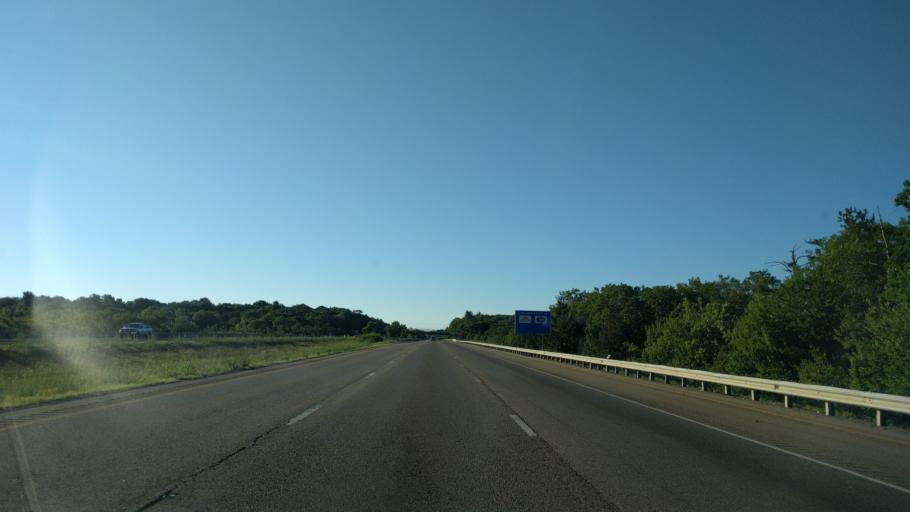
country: US
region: Massachusetts
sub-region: Norfolk County
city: Franklin
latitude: 42.0745
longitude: -71.4153
